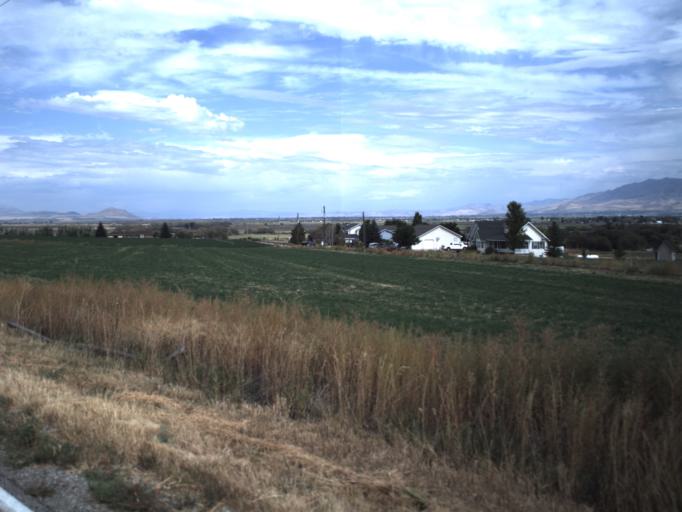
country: US
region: Utah
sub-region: Cache County
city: Wellsville
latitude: 41.6582
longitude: -111.9449
